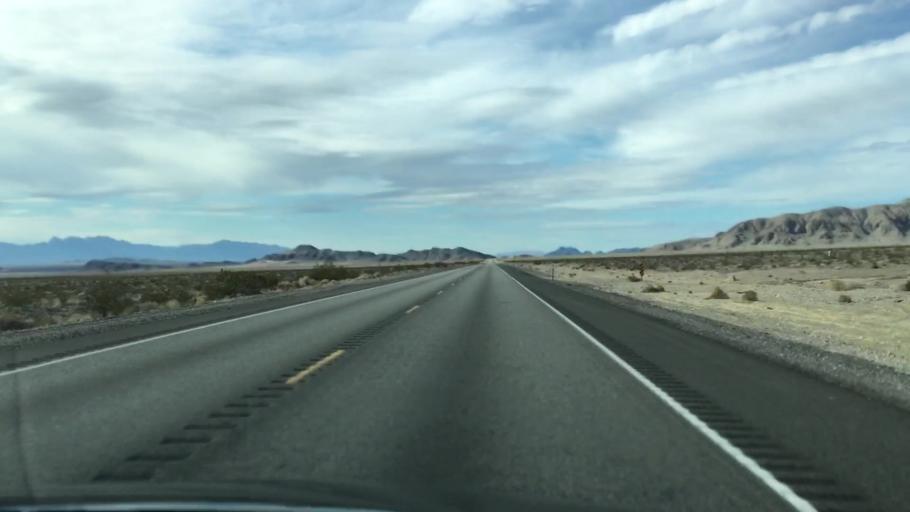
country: US
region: Nevada
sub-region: Nye County
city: Pahrump
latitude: 36.5689
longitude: -116.1524
